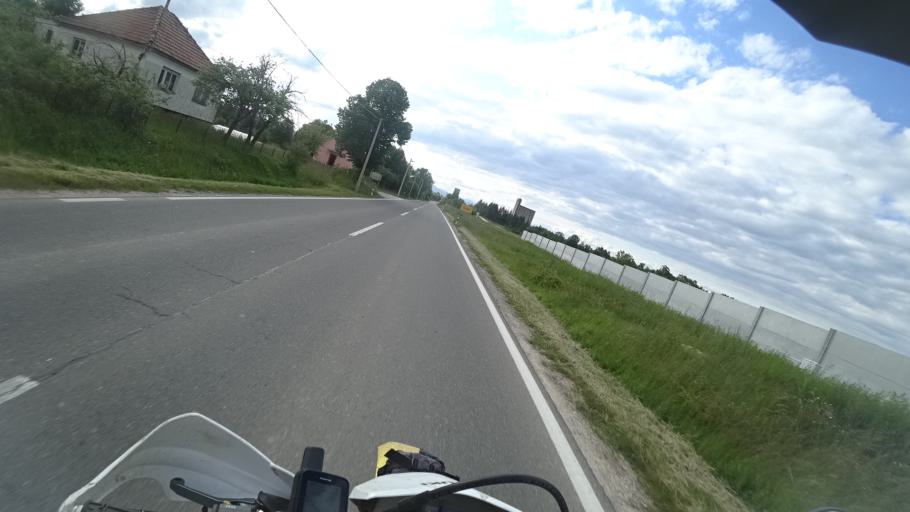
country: HR
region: Licko-Senjska
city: Gospic
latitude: 44.5300
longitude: 15.4035
